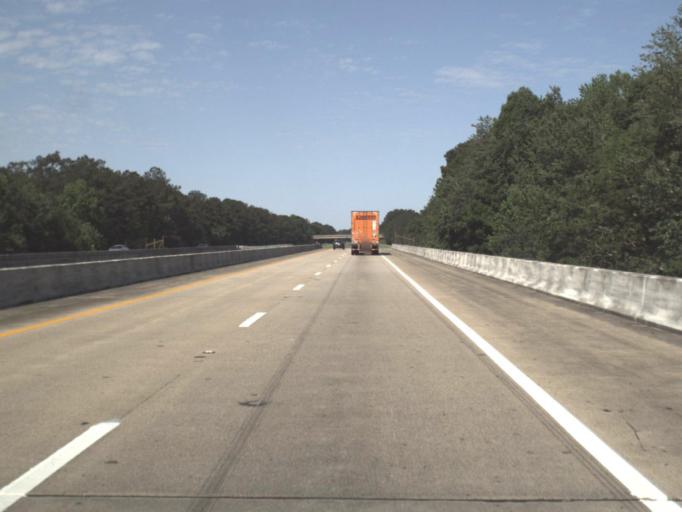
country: US
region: Florida
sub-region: Holmes County
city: Bonifay
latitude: 30.7539
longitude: -85.8425
